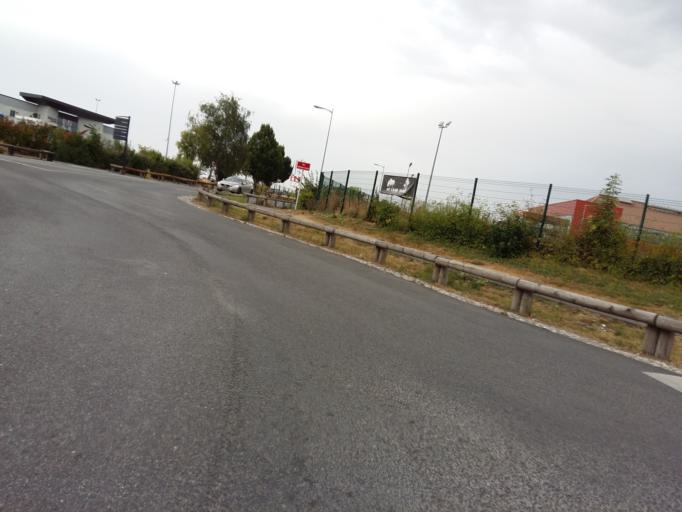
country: FR
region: Picardie
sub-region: Departement de la Somme
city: Camon
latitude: 49.8996
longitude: 2.3409
